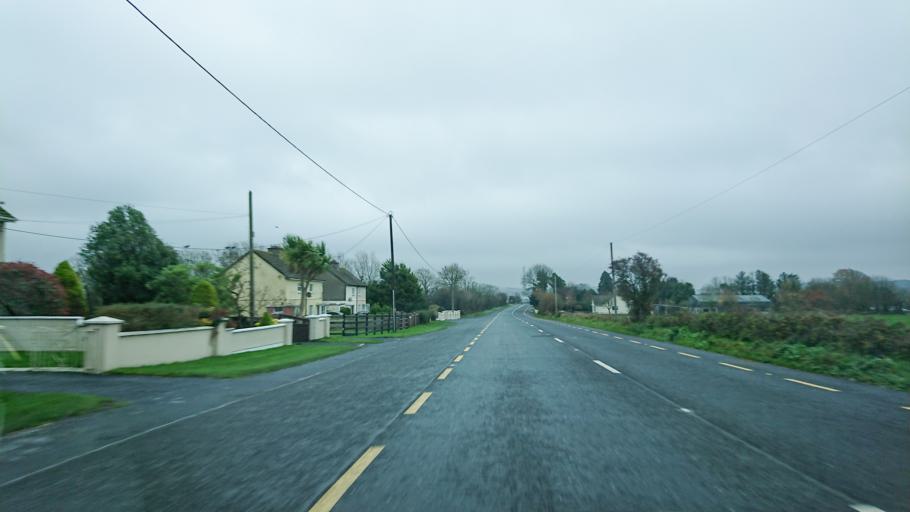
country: IE
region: Munster
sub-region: Waterford
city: Waterford
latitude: 52.2820
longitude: -7.1779
